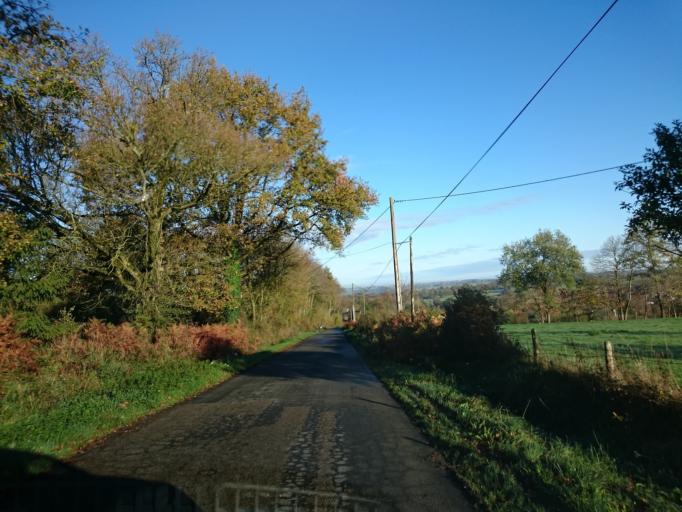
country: FR
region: Brittany
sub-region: Departement d'Ille-et-Vilaine
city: Chanteloup
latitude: 47.9272
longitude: -1.5869
